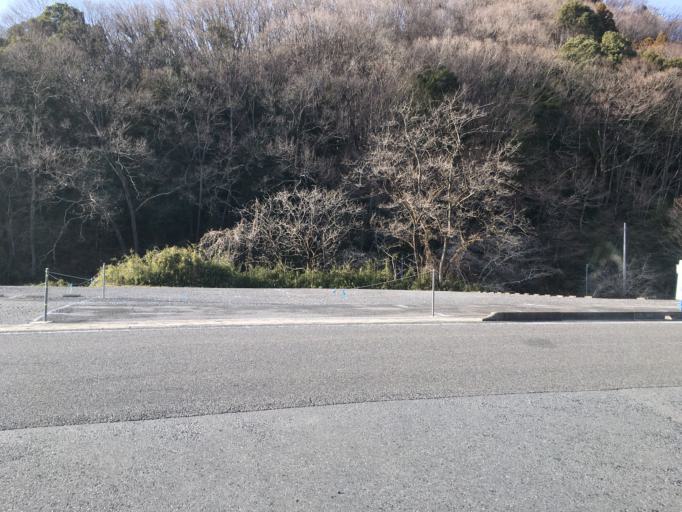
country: JP
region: Ibaraki
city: Daigo
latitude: 36.7630
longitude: 140.3984
